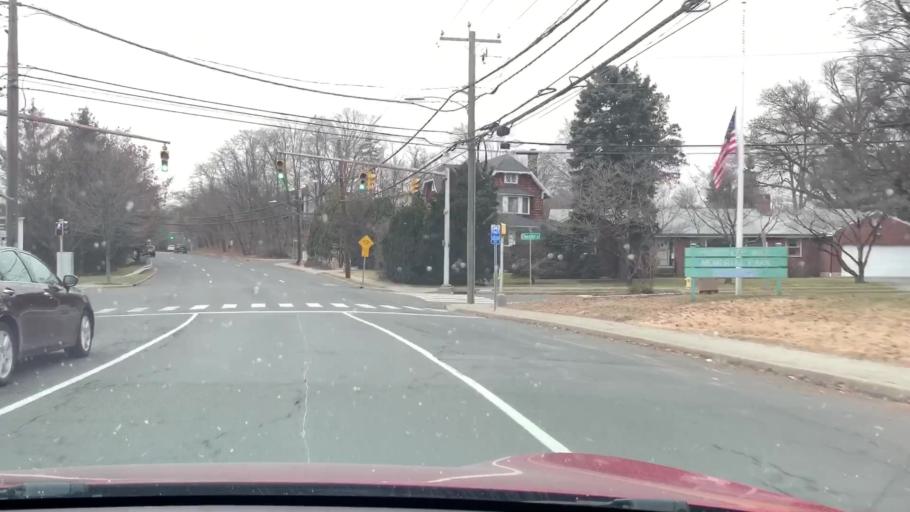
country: US
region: Connecticut
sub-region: Fairfield County
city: Stamford
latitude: 41.0671
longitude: -73.5428
